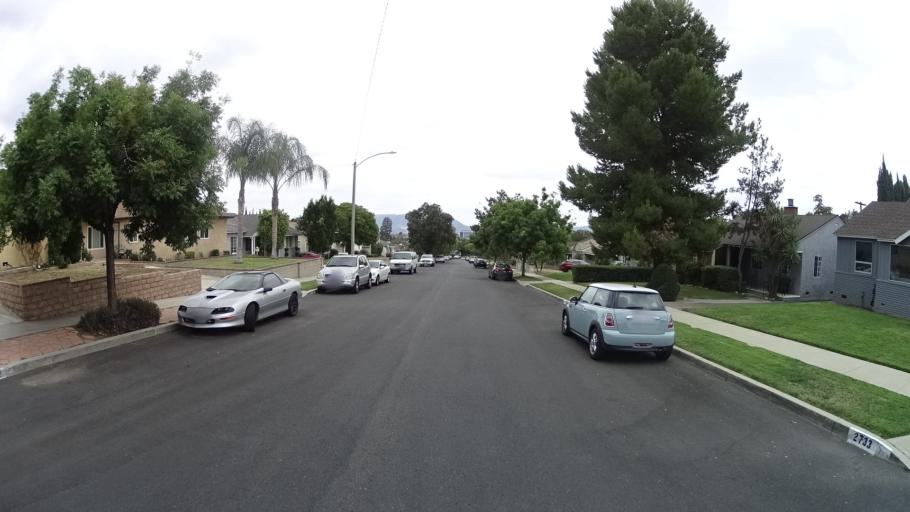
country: US
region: California
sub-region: Los Angeles County
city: Burbank
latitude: 34.2060
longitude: -118.3345
